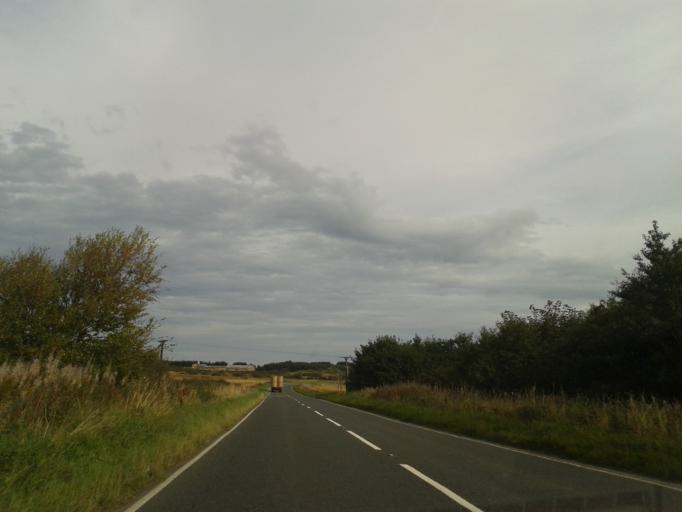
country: GB
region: Scotland
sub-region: Aberdeenshire
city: Turriff
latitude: 57.6004
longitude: -2.2804
